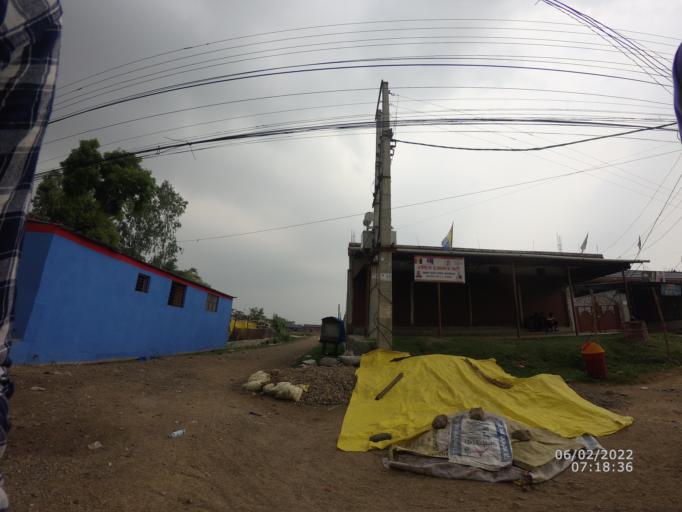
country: NP
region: Western Region
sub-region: Lumbini Zone
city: Bhairahawa
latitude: 27.4849
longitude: 83.4372
